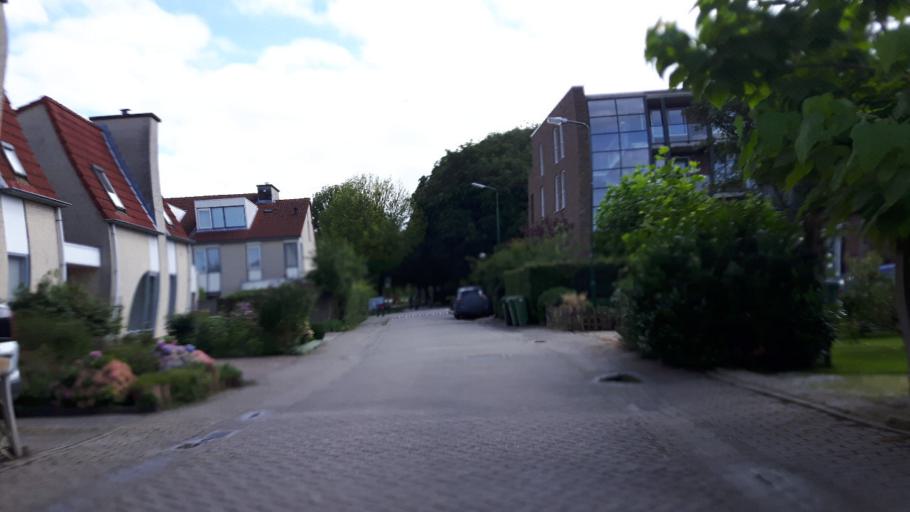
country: NL
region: Utrecht
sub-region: Gemeente IJsselstein
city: IJsselstein
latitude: 52.0240
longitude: 5.0413
